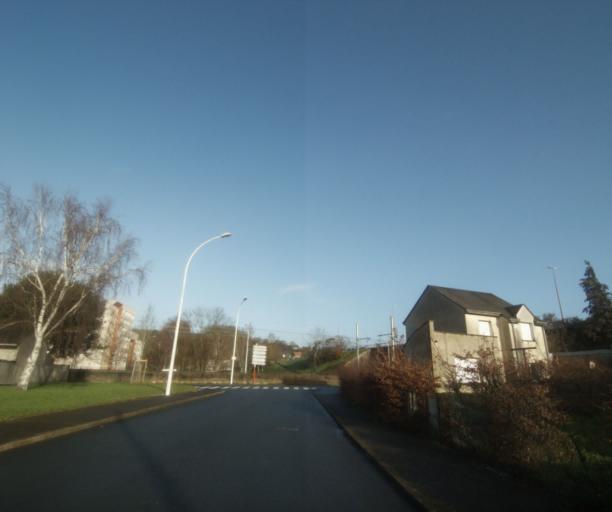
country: FR
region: Pays de la Loire
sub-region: Departement de la Sarthe
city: Le Mans
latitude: 47.9944
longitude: 0.2232
